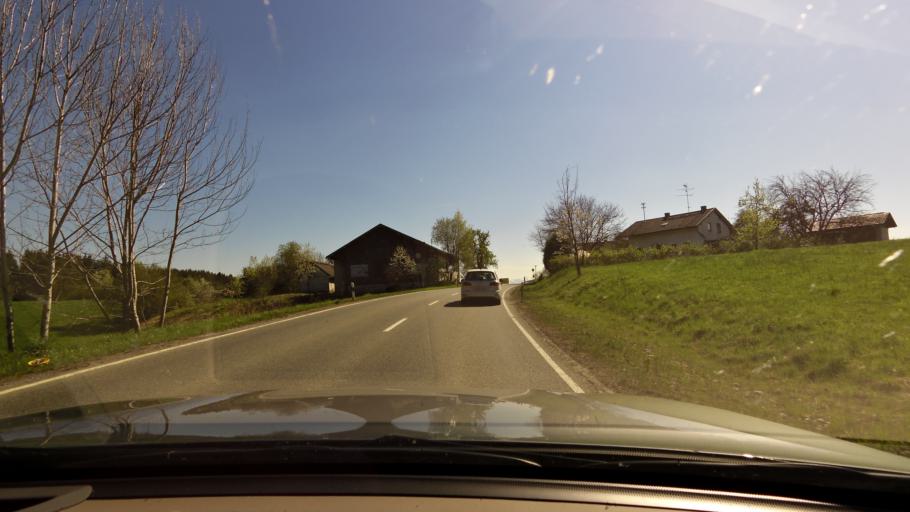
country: DE
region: Bavaria
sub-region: Upper Bavaria
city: Vogtareuth
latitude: 47.9576
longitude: 12.1821
